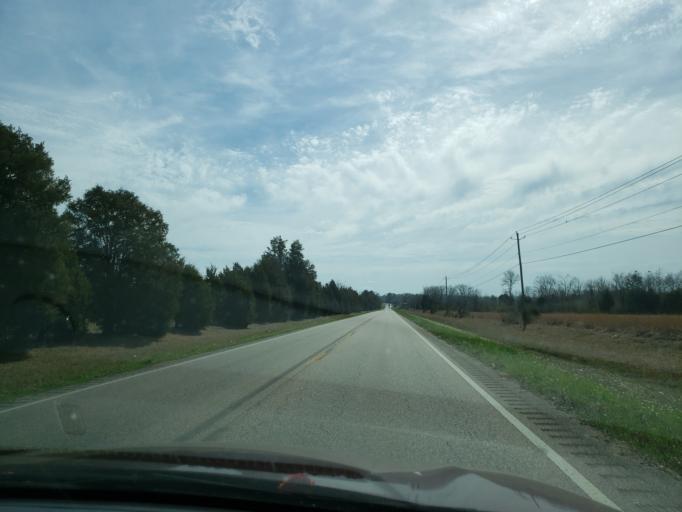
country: US
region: Alabama
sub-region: Dallas County
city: Selma
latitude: 32.4417
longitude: -87.0684
